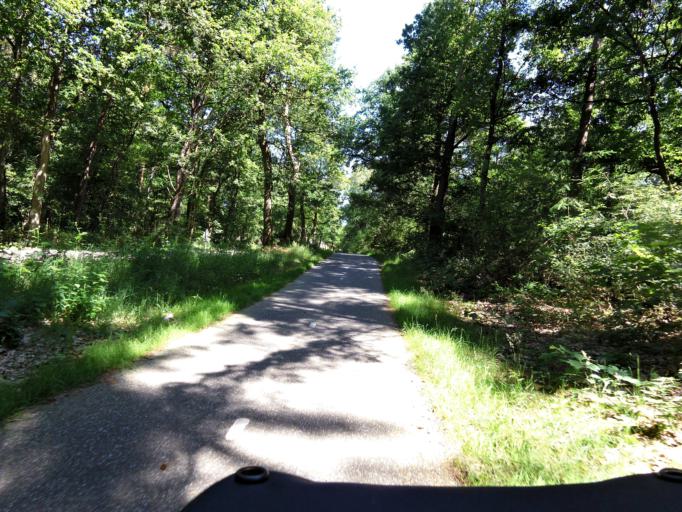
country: NL
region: Overijssel
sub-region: Gemeente Twenterand
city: Magele
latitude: 52.5088
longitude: 6.5146
